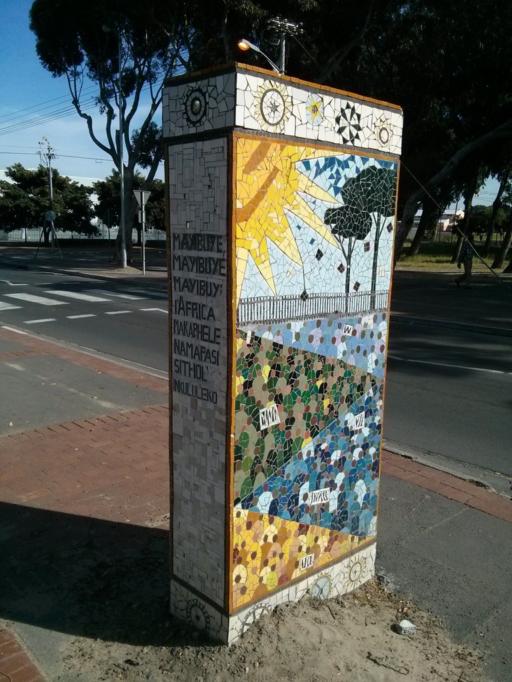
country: ZA
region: Western Cape
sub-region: City of Cape Town
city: Lansdowne
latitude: -33.9441
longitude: 18.5249
